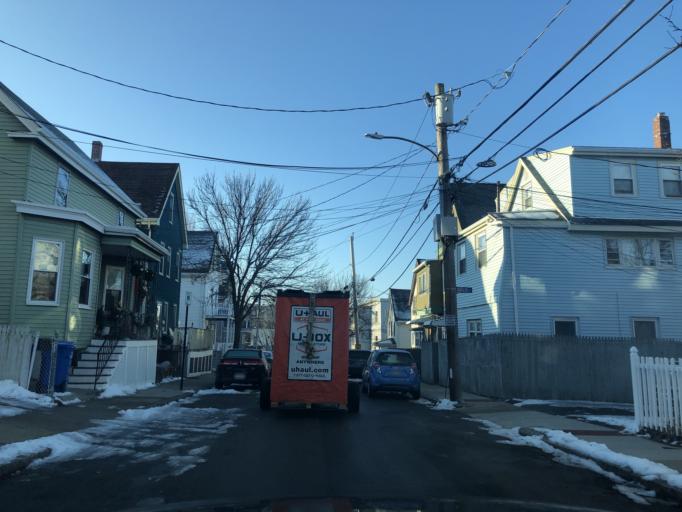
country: US
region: Massachusetts
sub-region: Middlesex County
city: Somerville
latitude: 42.3956
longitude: -71.1064
